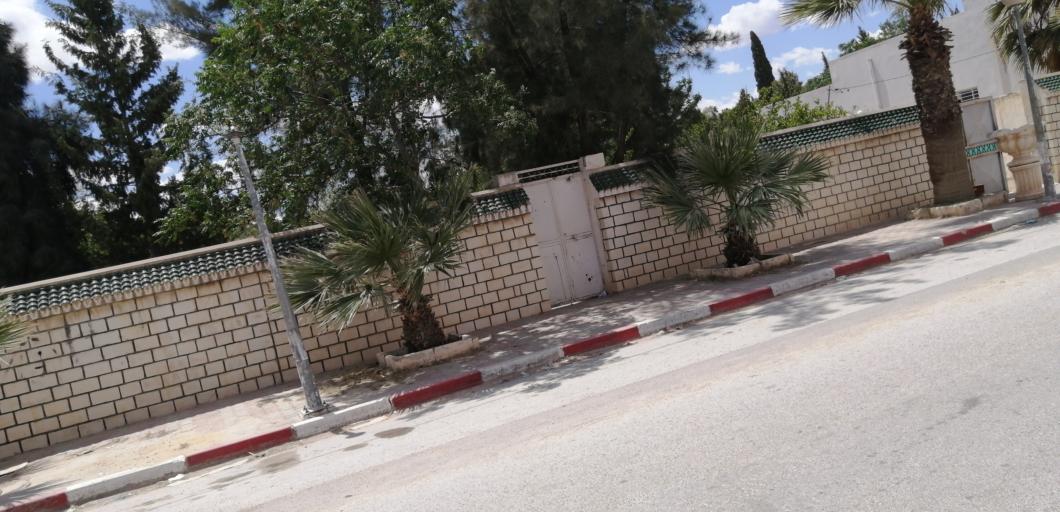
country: TN
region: Al Qayrawan
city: Kairouan
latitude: 35.6164
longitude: 9.9267
